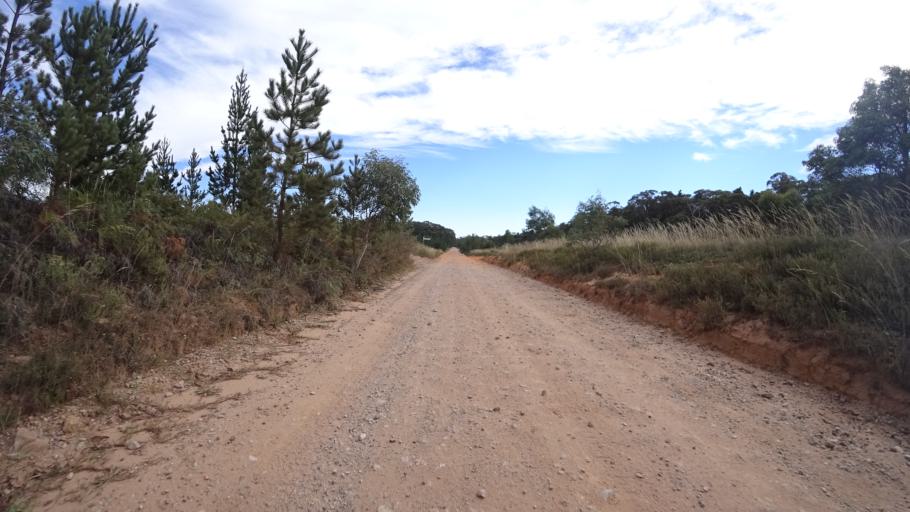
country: AU
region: New South Wales
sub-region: Lithgow
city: Lithgow
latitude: -33.3494
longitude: 150.2554
